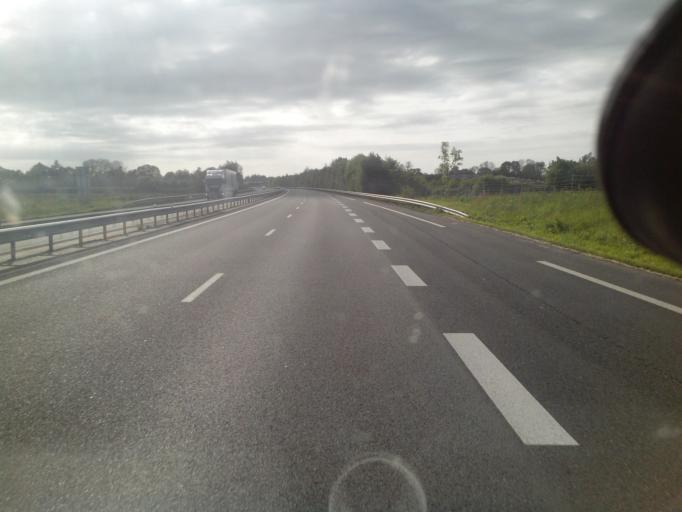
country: FR
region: Haute-Normandie
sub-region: Departement de l'Eure
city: Beuzeville
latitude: 49.3247
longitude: 0.3005
